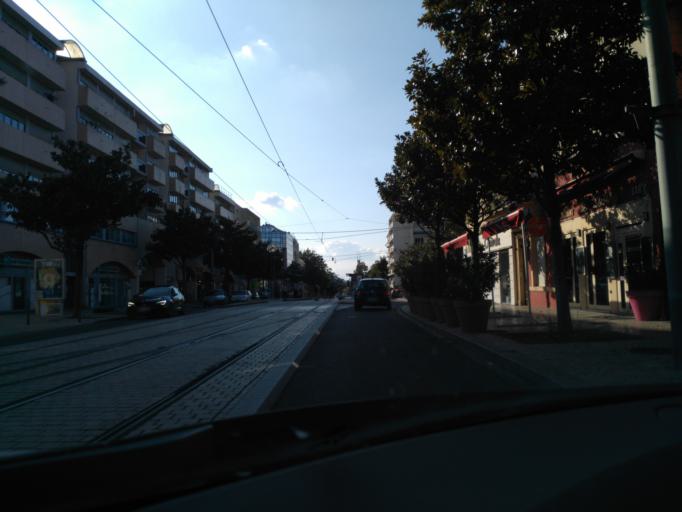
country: FR
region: Rhone-Alpes
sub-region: Departement du Rhone
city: Bron
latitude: 45.7331
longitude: 4.9100
